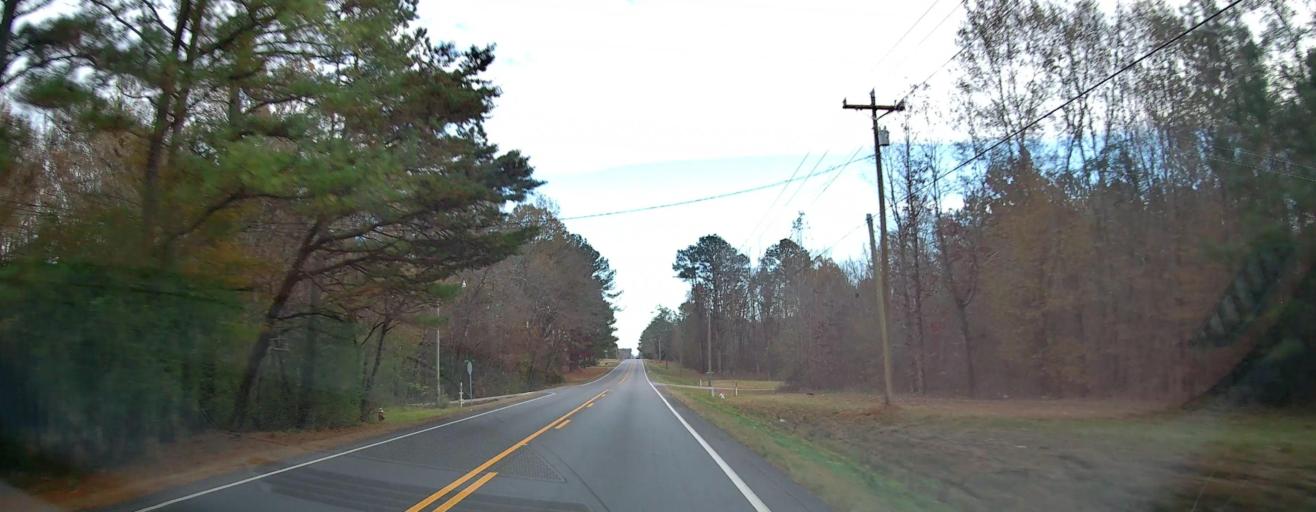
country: US
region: Alabama
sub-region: Morgan County
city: Priceville
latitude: 34.4602
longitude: -86.7785
